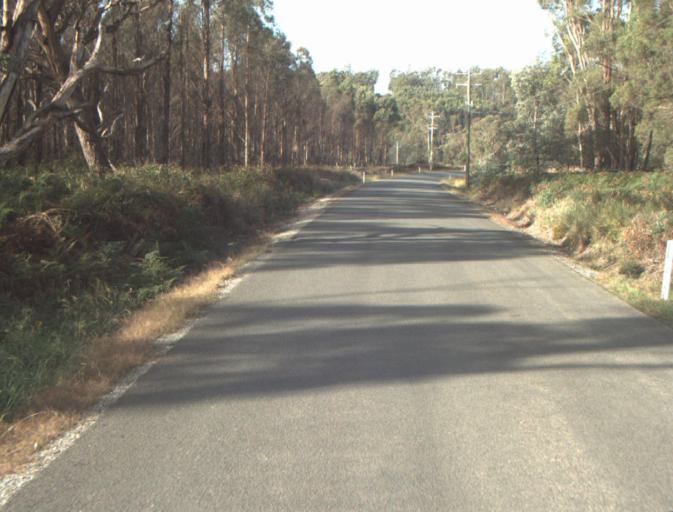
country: AU
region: Tasmania
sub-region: Launceston
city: Mayfield
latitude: -41.2377
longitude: 147.1806
